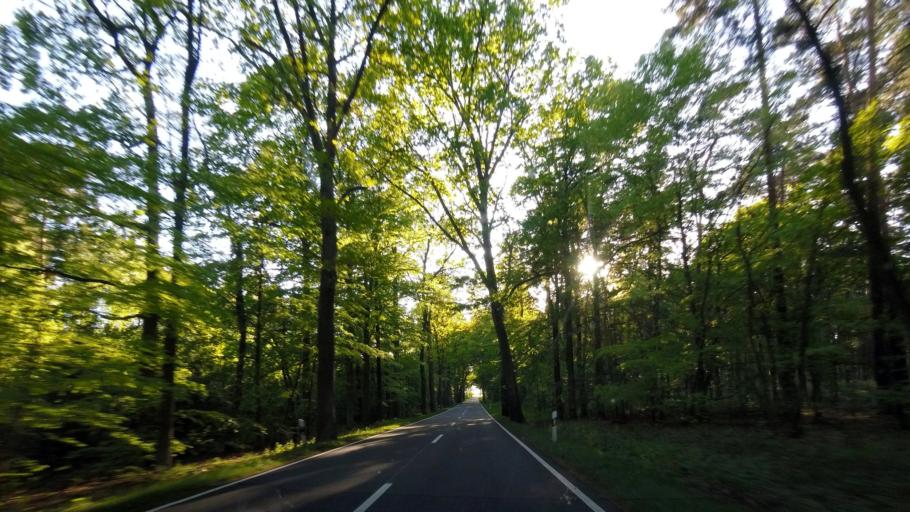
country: DE
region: Brandenburg
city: Ihlow
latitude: 51.9926
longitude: 13.3767
